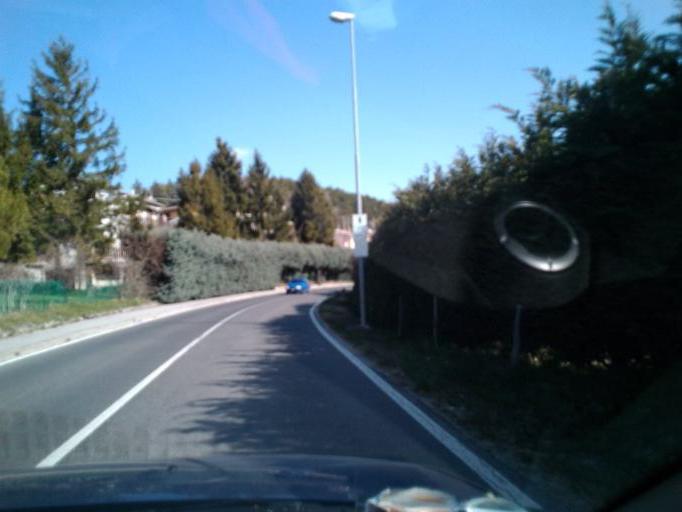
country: IT
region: Veneto
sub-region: Provincia di Verona
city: Cerro Veronese
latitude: 45.5664
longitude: 11.0412
